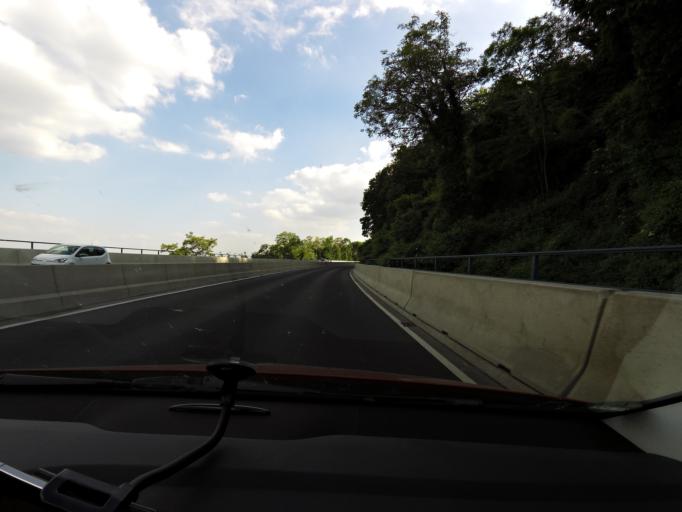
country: DE
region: Rheinland-Pfalz
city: Leutesdorf
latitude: 50.4407
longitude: 7.3924
